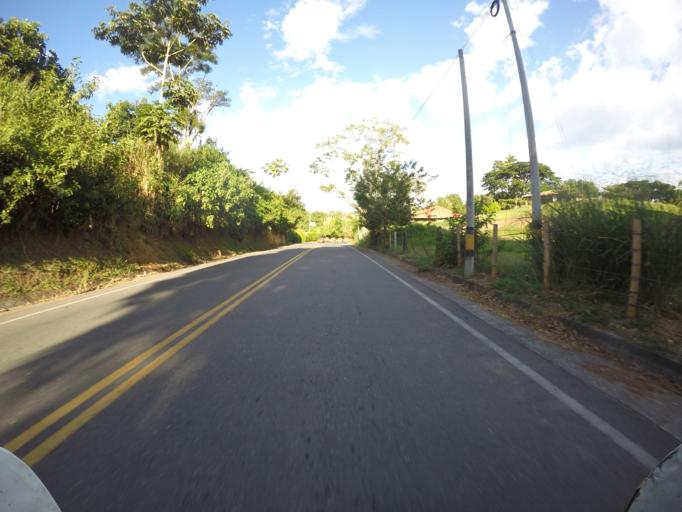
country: CO
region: Valle del Cauca
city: Alcala
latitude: 4.7017
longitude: -75.8340
